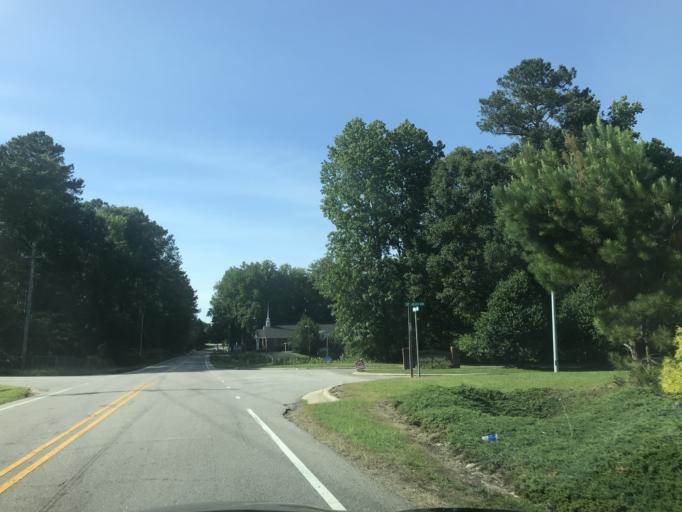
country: US
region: North Carolina
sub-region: Johnston County
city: Clayton
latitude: 35.6198
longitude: -78.5361
